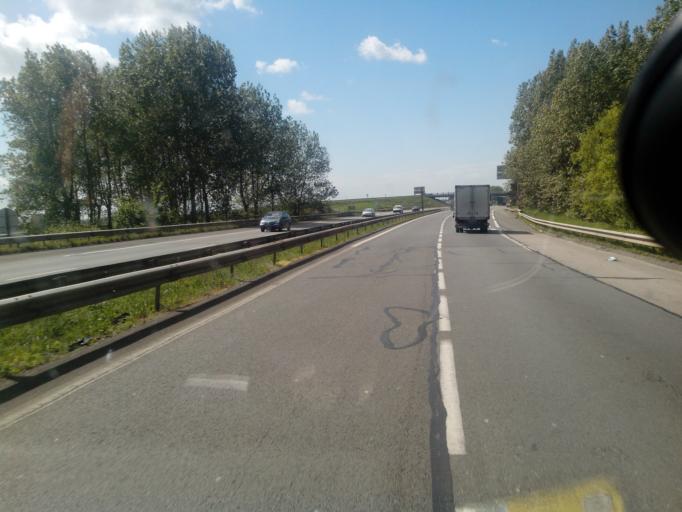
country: FR
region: Nord-Pas-de-Calais
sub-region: Departement du Nord
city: Cappelle-la-Grande
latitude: 50.9922
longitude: 2.3408
